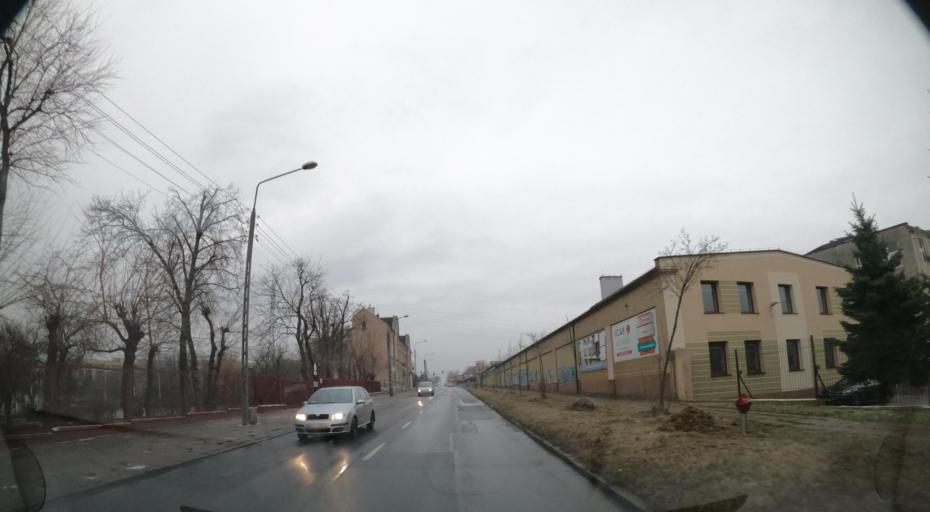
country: PL
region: Masovian Voivodeship
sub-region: Radom
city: Radom
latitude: 51.3843
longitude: 21.1229
